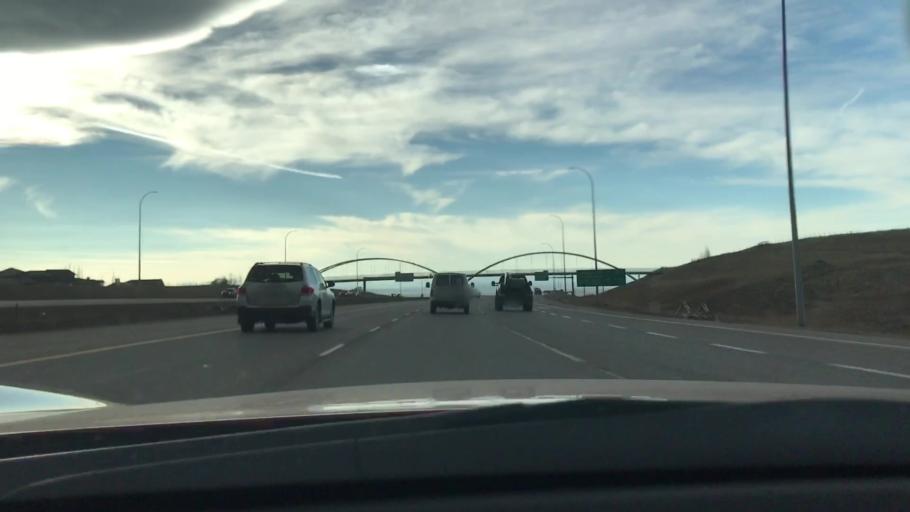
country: CA
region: Alberta
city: Calgary
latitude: 51.1401
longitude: -114.2100
